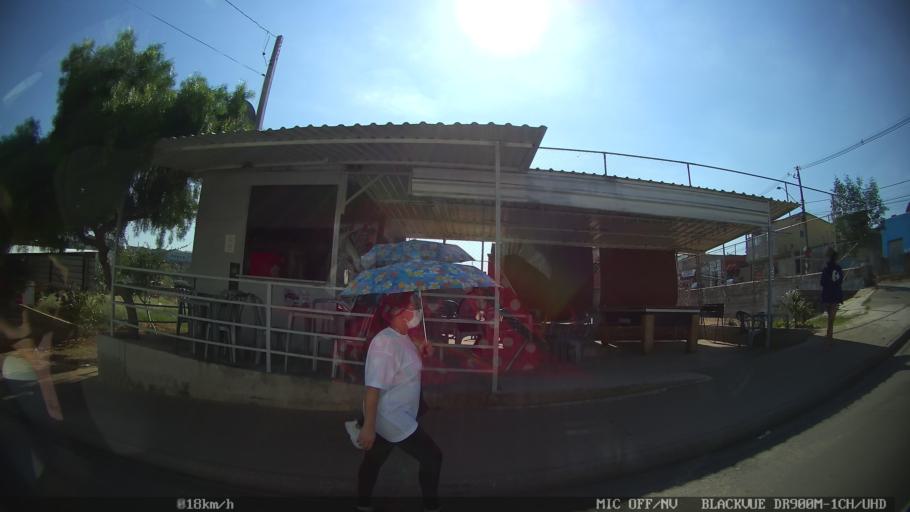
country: BR
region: Sao Paulo
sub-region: Campinas
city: Campinas
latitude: -22.9451
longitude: -47.0834
